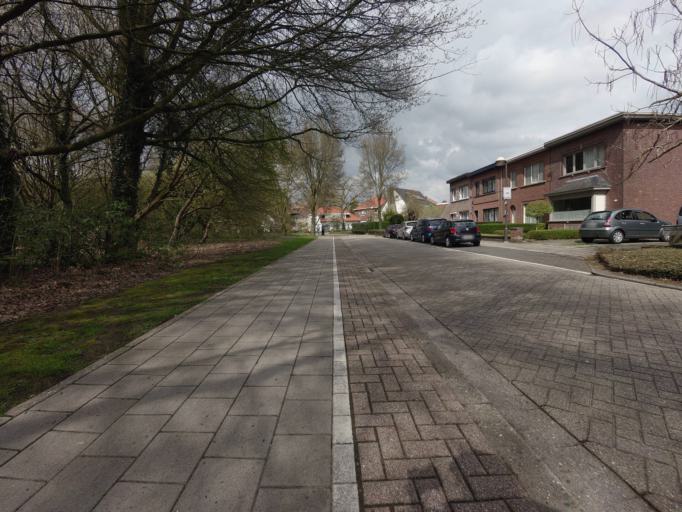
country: BE
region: Flanders
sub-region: Provincie Antwerpen
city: Mortsel
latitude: 51.1732
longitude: 4.4658
